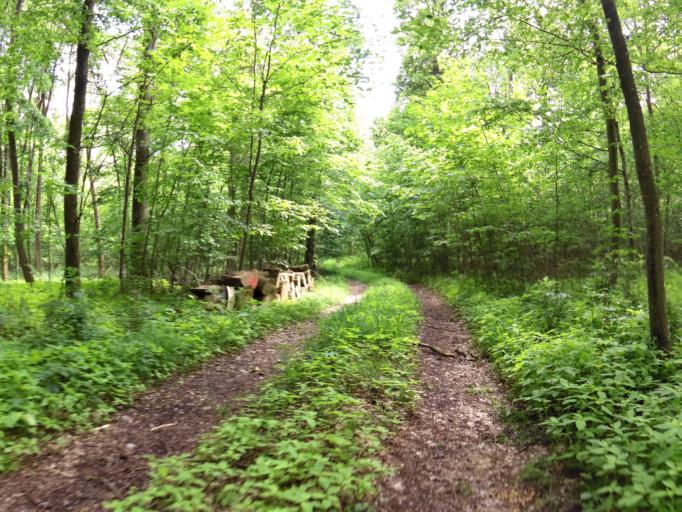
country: DE
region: Bavaria
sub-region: Regierungsbezirk Unterfranken
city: Theilheim
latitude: 49.7326
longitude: 10.0624
